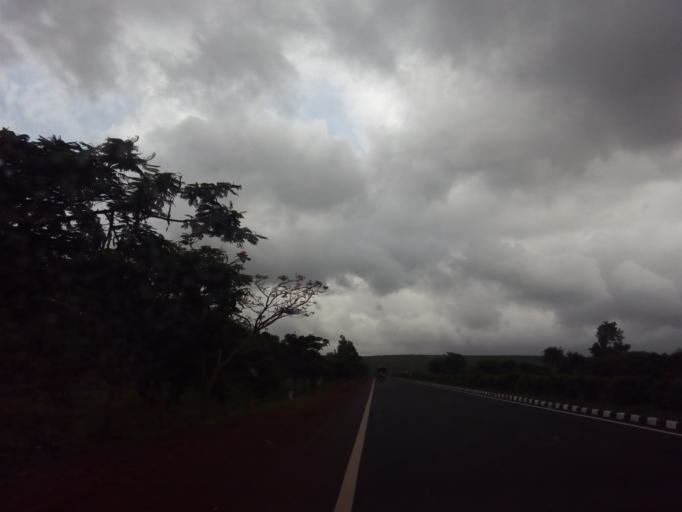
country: IN
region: Karnataka
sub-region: Belgaum
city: Hukeri
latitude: 16.0587
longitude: 74.5138
